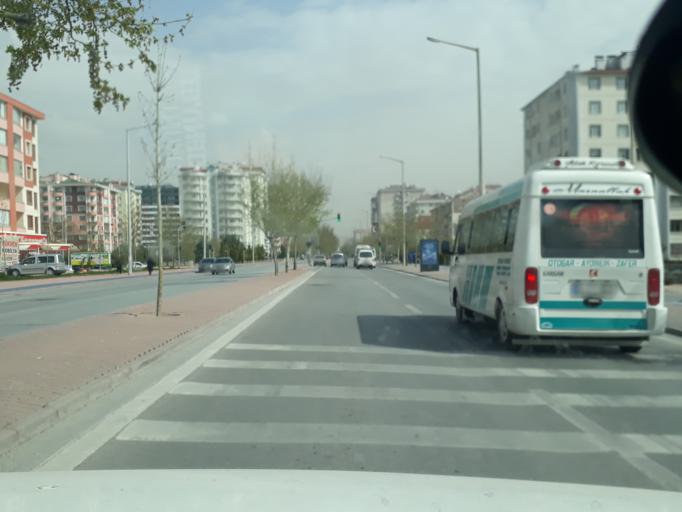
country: TR
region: Konya
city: Selcuklu
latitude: 37.9414
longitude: 32.4931
